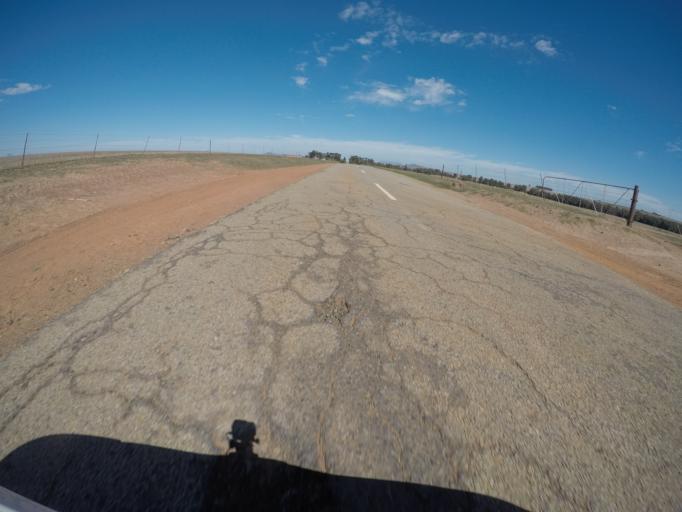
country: ZA
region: Western Cape
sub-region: City of Cape Town
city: Atlantis
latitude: -33.6059
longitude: 18.6393
